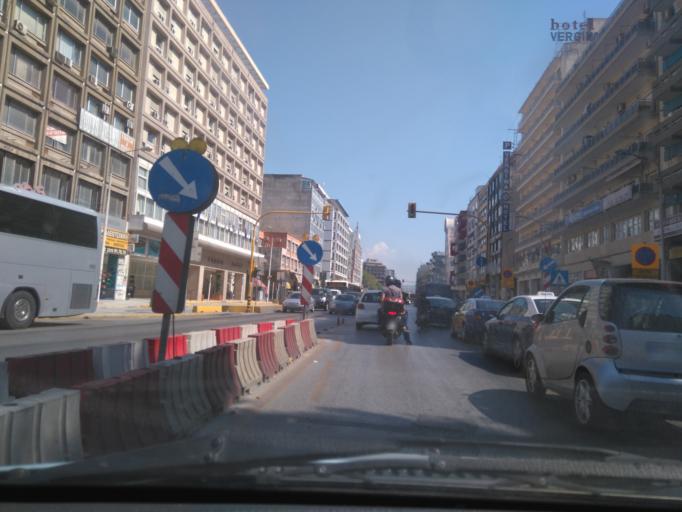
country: GR
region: Central Macedonia
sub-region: Nomos Thessalonikis
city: Thessaloniki
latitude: 40.6421
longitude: 22.9318
